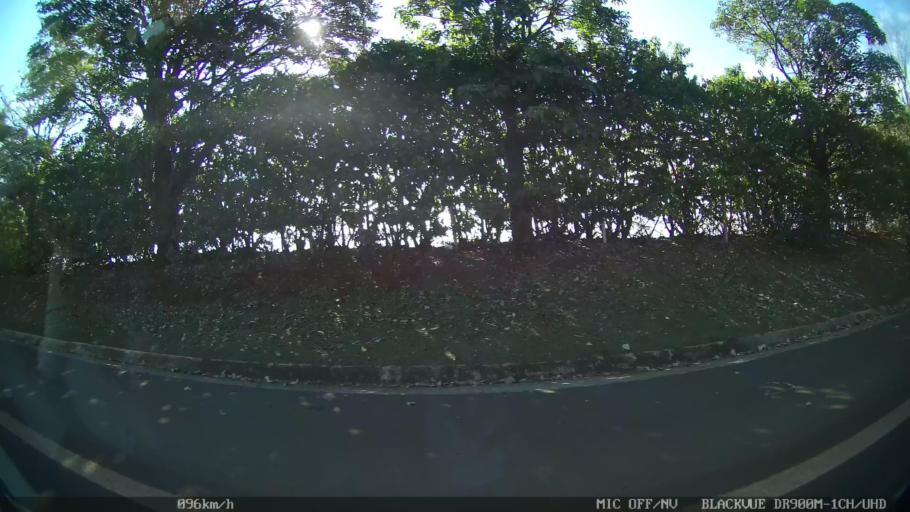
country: BR
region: Sao Paulo
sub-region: Iracemapolis
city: Iracemapolis
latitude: -22.6692
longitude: -47.5513
